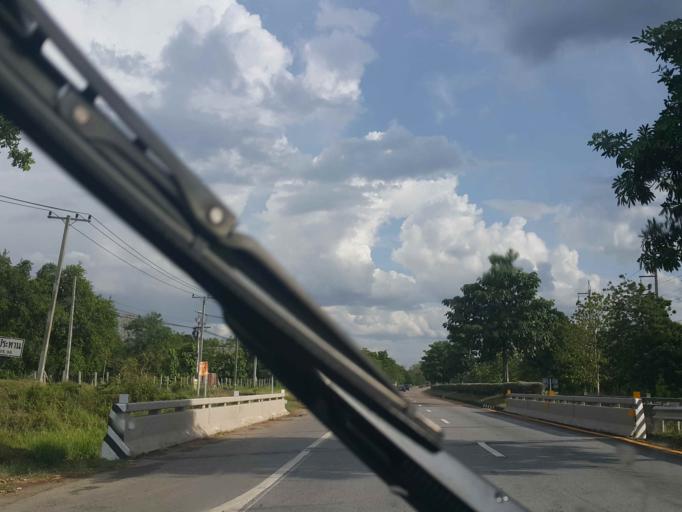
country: TH
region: Phrae
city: Sung Men
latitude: 18.0091
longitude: 100.1054
